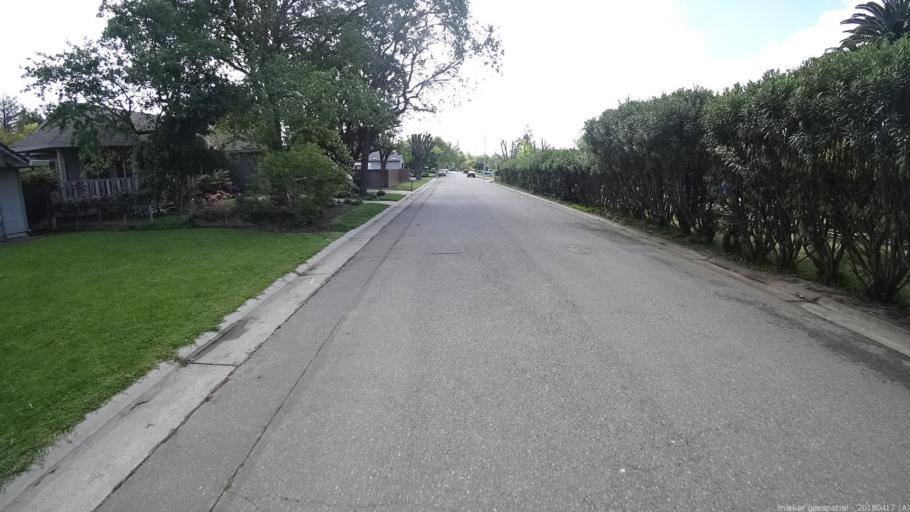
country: US
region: California
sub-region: Sacramento County
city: Walnut Grove
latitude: 38.2486
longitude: -121.5164
